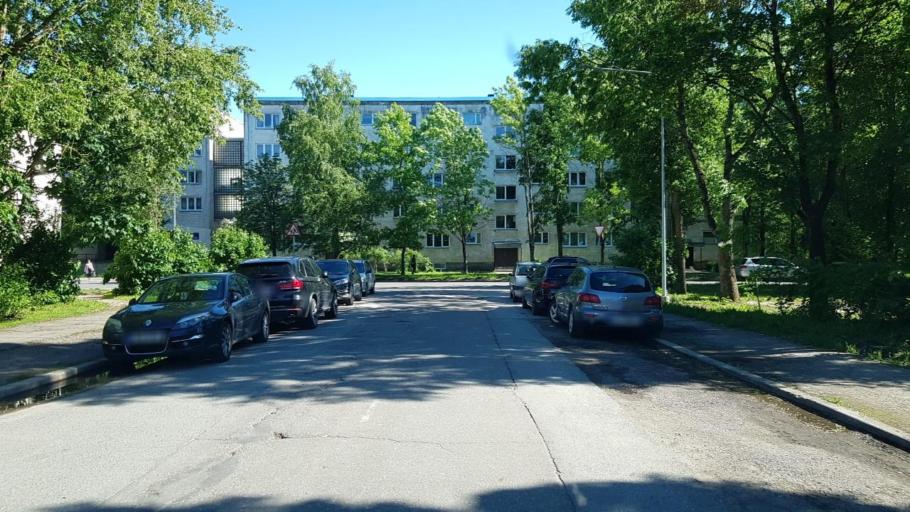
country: EE
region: Ida-Virumaa
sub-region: Narva linn
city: Narva
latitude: 59.3695
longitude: 28.1770
